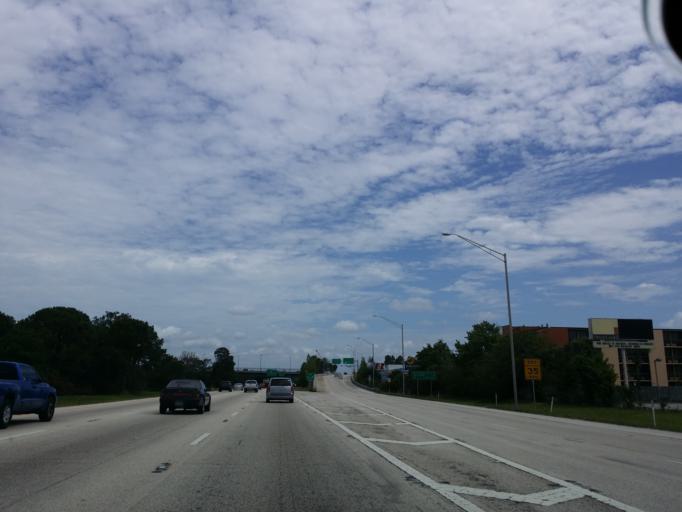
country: US
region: Florida
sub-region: Orange County
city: Tangelo Park
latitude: 28.4629
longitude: -81.4681
